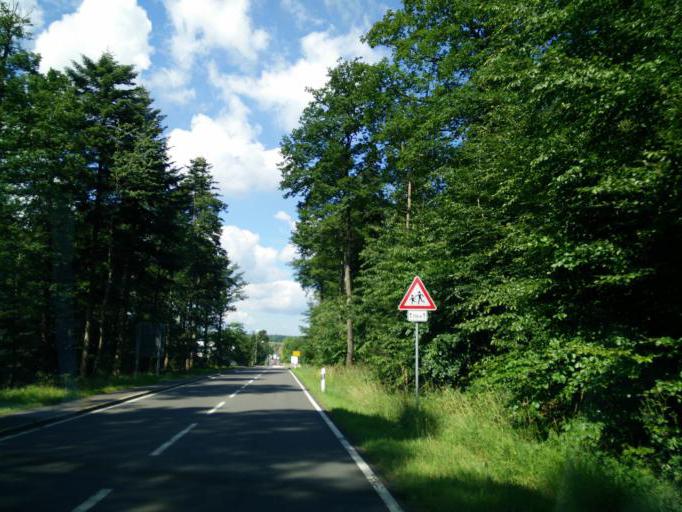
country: DE
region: Baden-Wuerttemberg
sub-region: Karlsruhe Region
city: Engelsbrand
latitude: 48.8312
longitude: 8.6562
